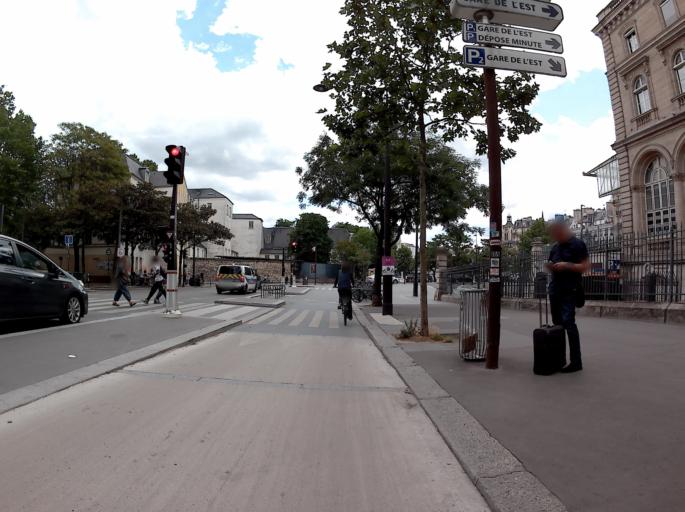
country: FR
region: Ile-de-France
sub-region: Paris
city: Paris
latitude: 48.8766
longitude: 2.3608
